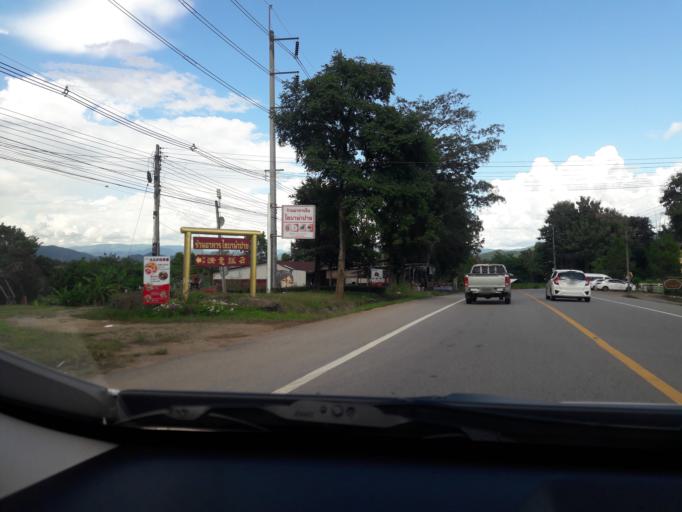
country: TH
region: Mae Hong Son
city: Mae Hi
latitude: 19.3383
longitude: 98.4328
